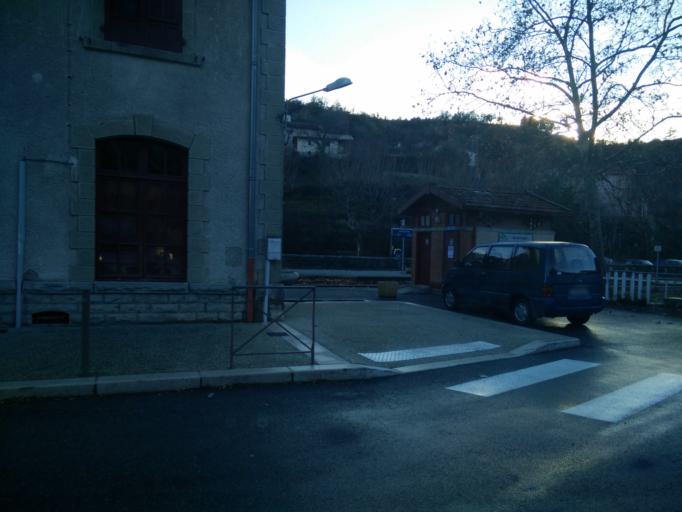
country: FR
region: Provence-Alpes-Cote d'Azur
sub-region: Departement des Alpes-Maritimes
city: Puget-Theniers
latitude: 43.9493
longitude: 6.8129
